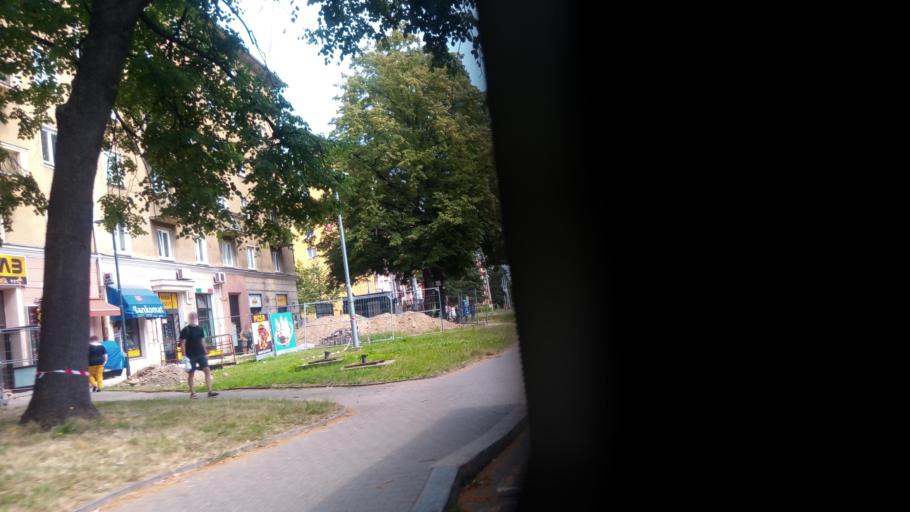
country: CZ
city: Vresina
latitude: 49.8320
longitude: 18.1754
